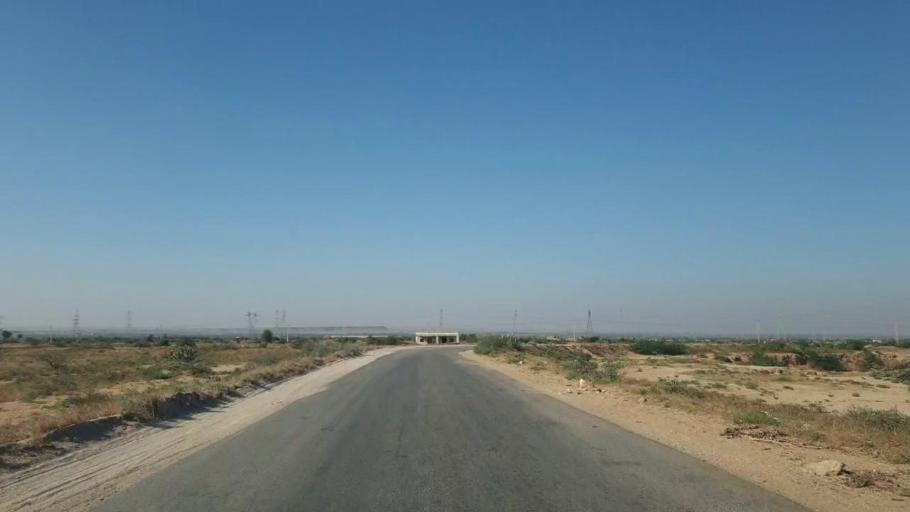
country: PK
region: Sindh
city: Gharo
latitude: 25.1686
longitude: 67.6605
